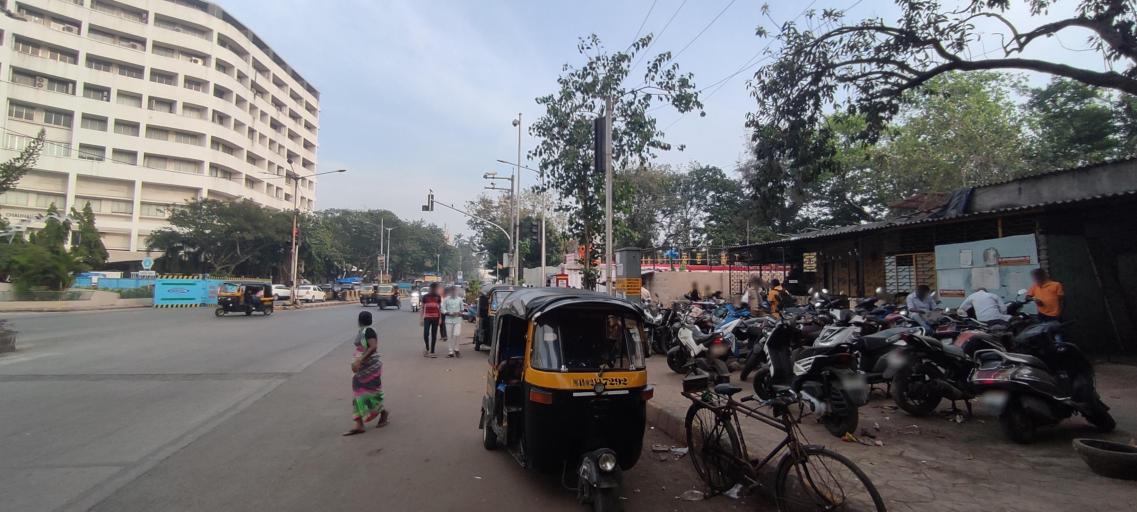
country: IN
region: Maharashtra
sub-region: Mumbai Suburban
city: Mumbai
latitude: 19.1026
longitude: 72.8366
